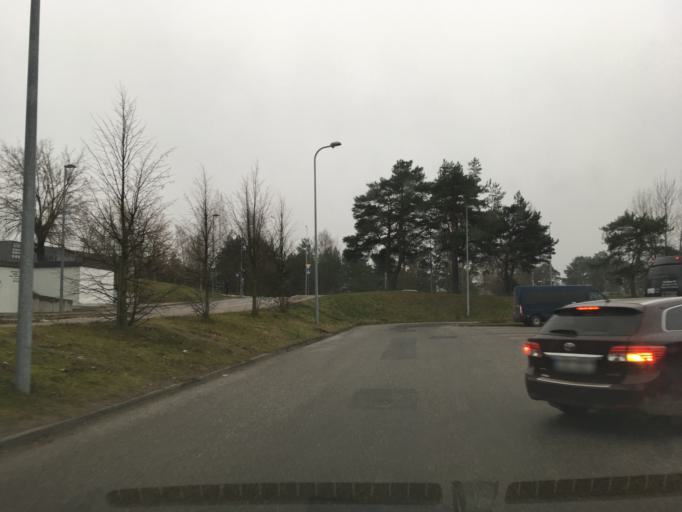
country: EE
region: Harju
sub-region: Tallinna linn
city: Tallinn
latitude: 59.4011
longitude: 24.7155
